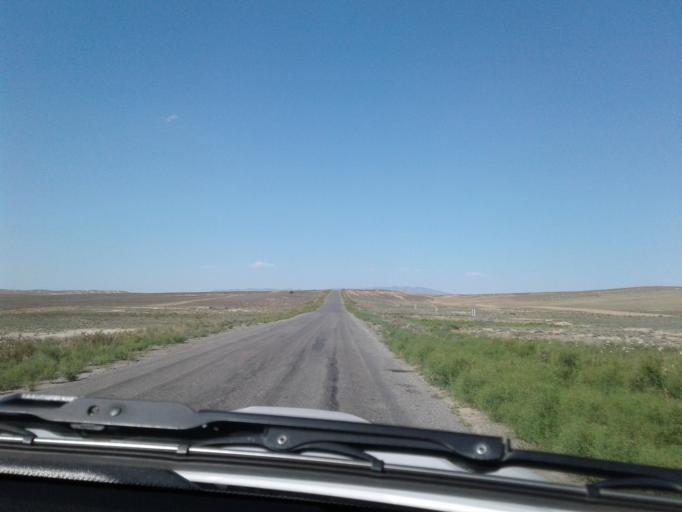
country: TM
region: Balkan
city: Magtymguly
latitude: 38.6321
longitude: 56.2431
